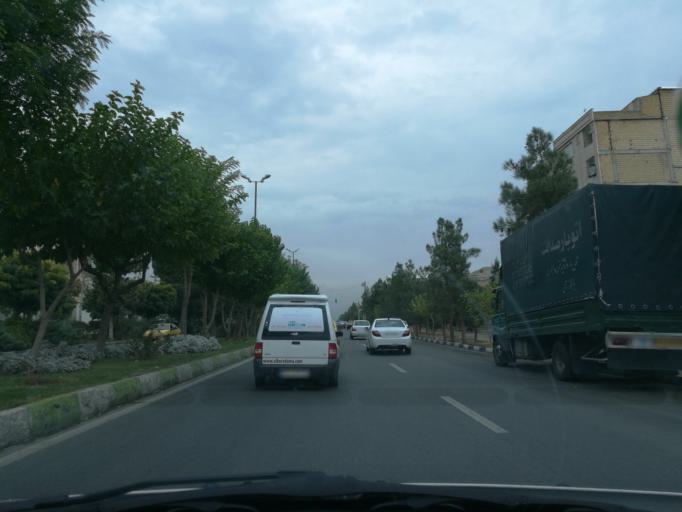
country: IR
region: Alborz
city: Karaj
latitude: 35.8606
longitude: 50.9405
